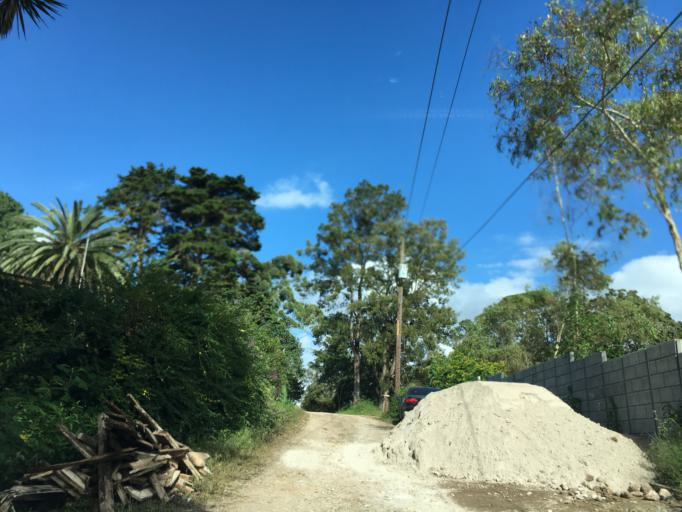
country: GT
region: Guatemala
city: San Jose Pinula
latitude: 14.6057
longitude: -90.4310
